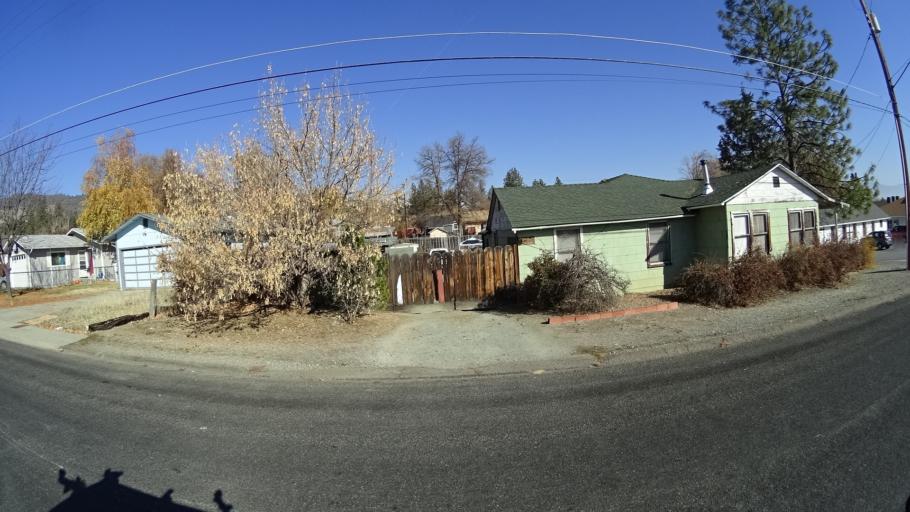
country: US
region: California
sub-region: Siskiyou County
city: Yreka
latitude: 41.7344
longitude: -122.6491
